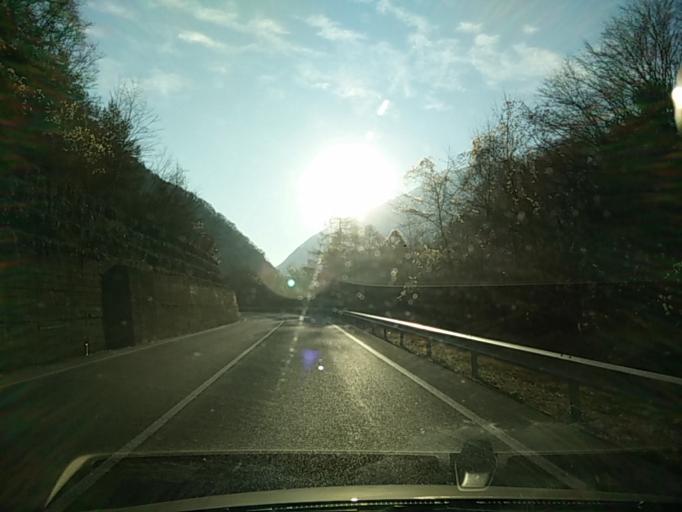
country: IT
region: Veneto
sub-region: Provincia di Belluno
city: Farra d'Alpago
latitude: 46.0997
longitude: 12.3470
